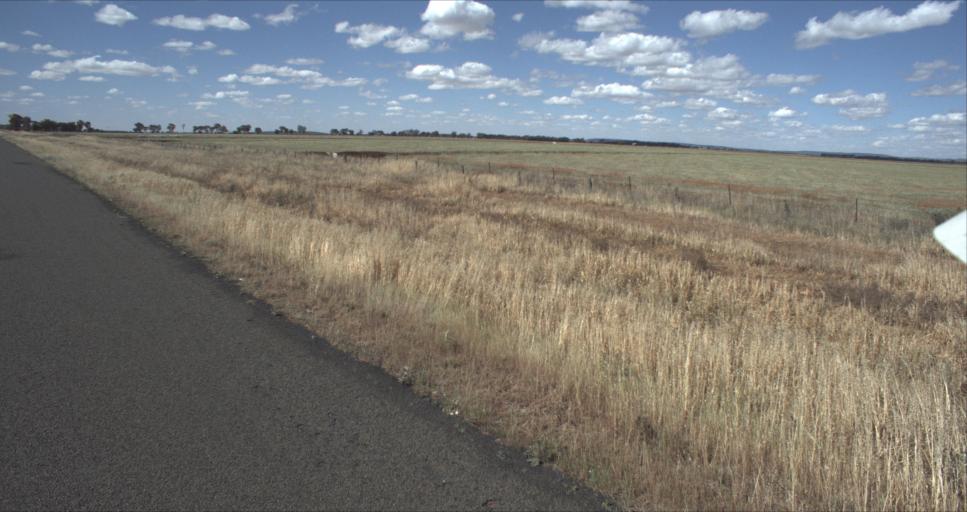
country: AU
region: New South Wales
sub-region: Leeton
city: Leeton
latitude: -34.4674
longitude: 146.2516
